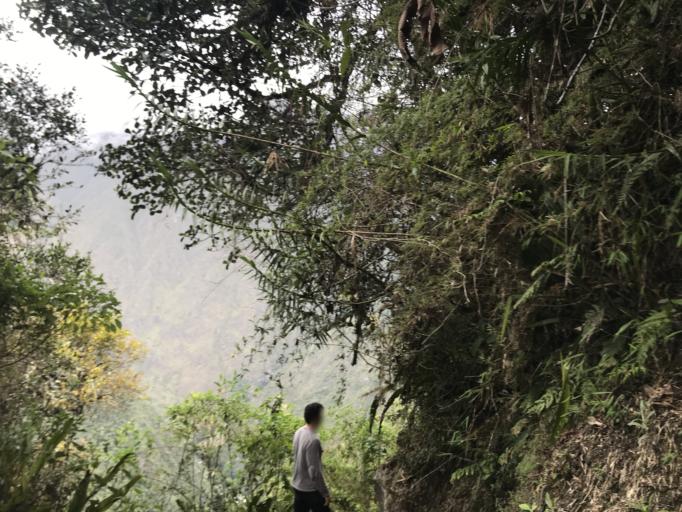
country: PE
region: Cusco
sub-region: Provincia de La Convencion
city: Santa Teresa
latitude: -13.1744
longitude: -72.5354
